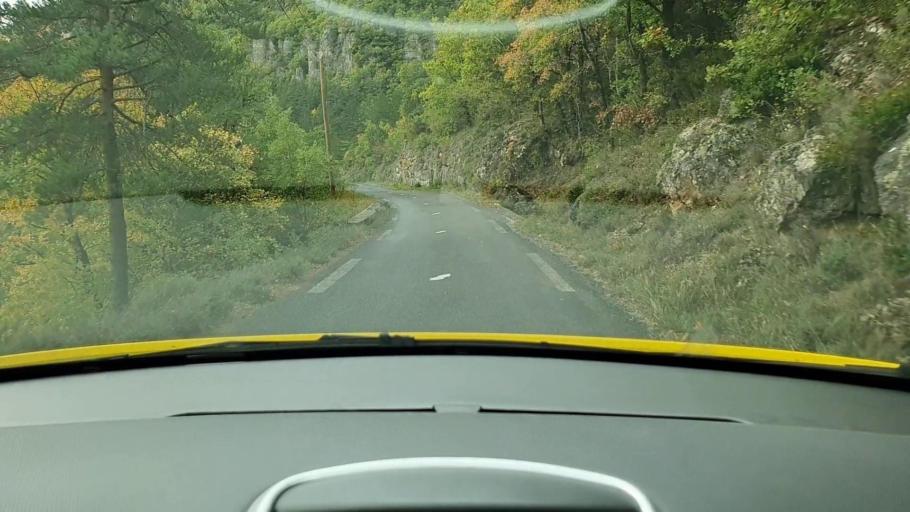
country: FR
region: Languedoc-Roussillon
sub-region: Departement de la Lozere
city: Meyrueis
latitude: 44.0895
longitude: 3.3976
